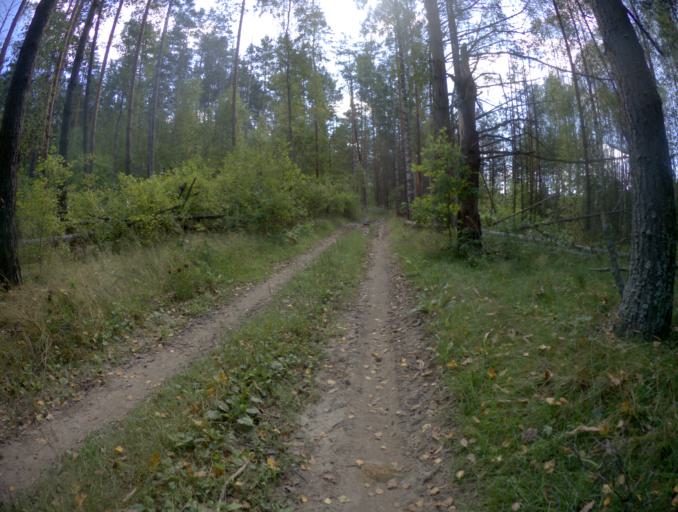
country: RU
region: Vladimir
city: Krasnaya Gorbatka
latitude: 55.9914
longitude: 41.8855
